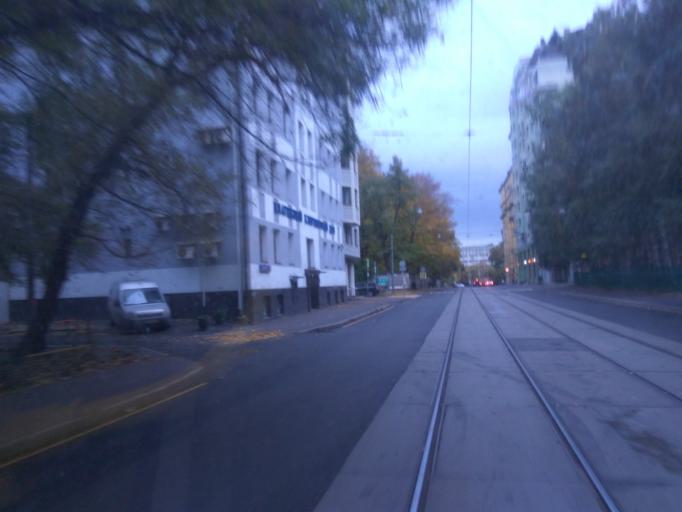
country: RU
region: Moscow
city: Mar'ina Roshcha
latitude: 55.7868
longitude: 37.6083
